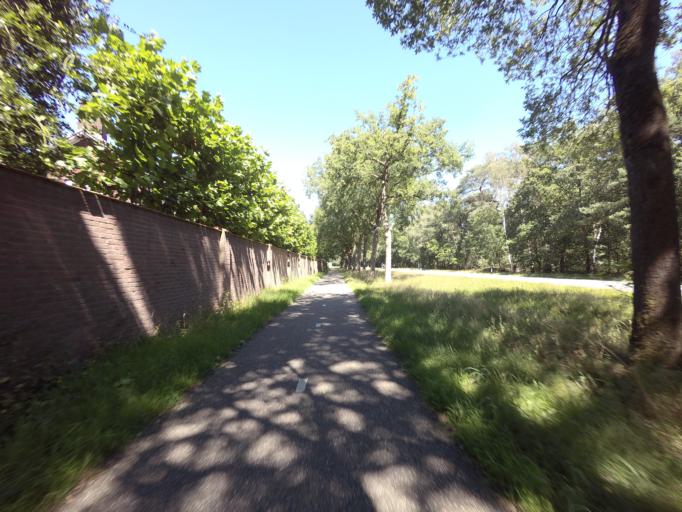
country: NL
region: Utrecht
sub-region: Gemeente Zeist
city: Zeist
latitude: 52.1325
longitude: 5.2498
